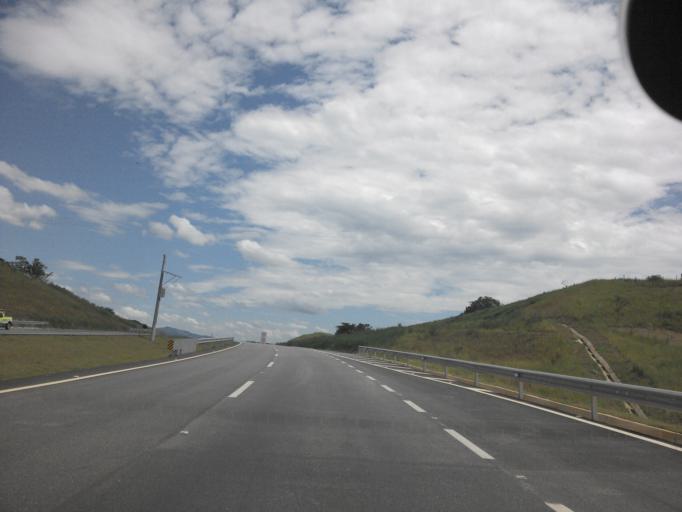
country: BR
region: Sao Paulo
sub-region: Taubate
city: Taubate
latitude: -23.0939
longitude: -45.5833
